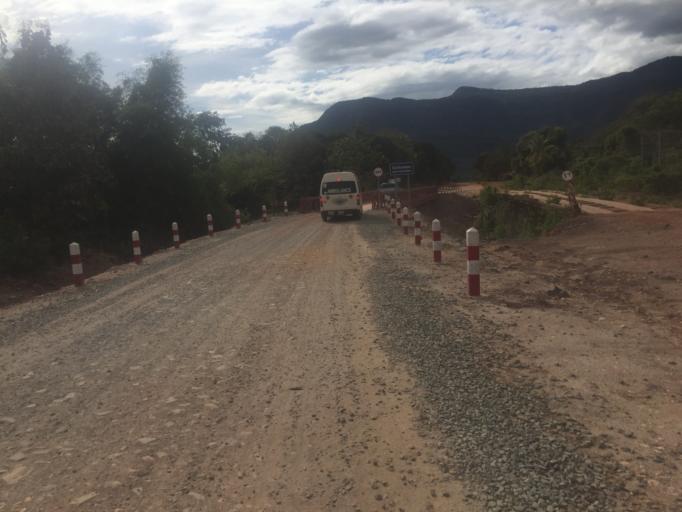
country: LA
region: Attapu
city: Attapu
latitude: 14.8077
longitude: 106.7665
